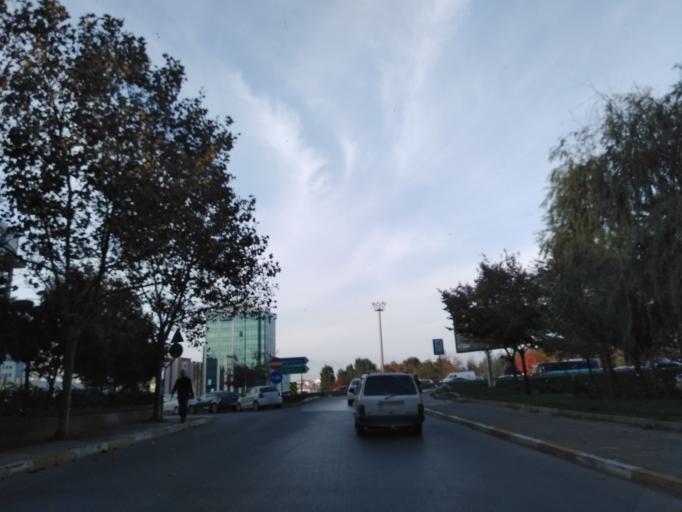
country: TR
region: Istanbul
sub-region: Atasehir
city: Atasehir
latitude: 40.9806
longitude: 29.0926
